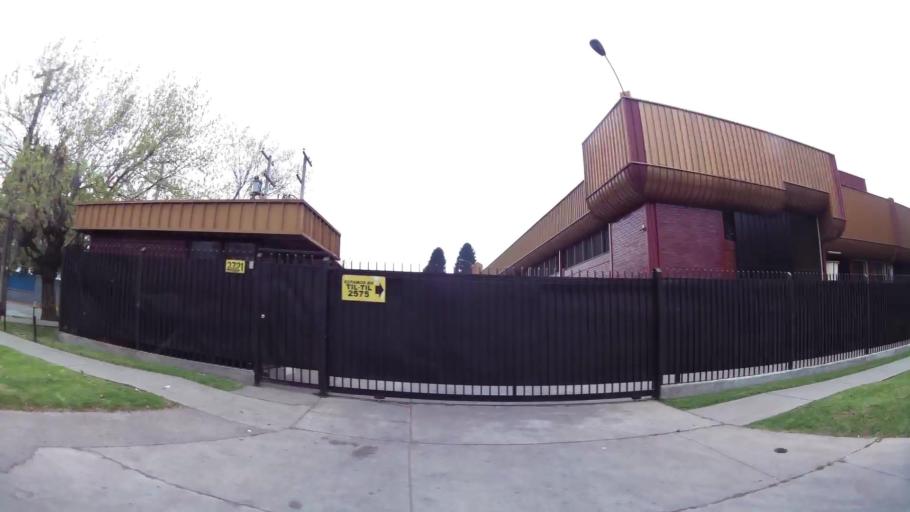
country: CL
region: Santiago Metropolitan
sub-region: Provincia de Santiago
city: Santiago
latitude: -33.4808
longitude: -70.6172
